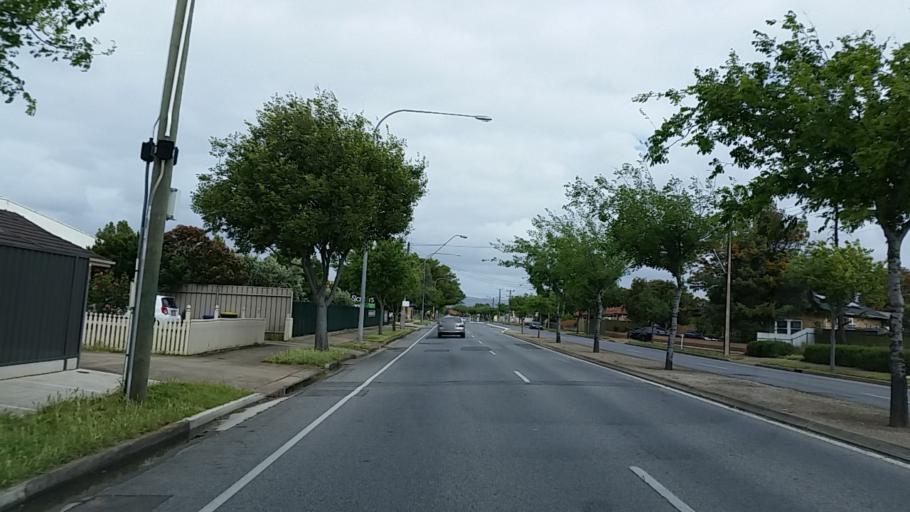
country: AU
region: South Australia
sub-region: Charles Sturt
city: Findon
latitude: -34.9013
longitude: 138.5412
